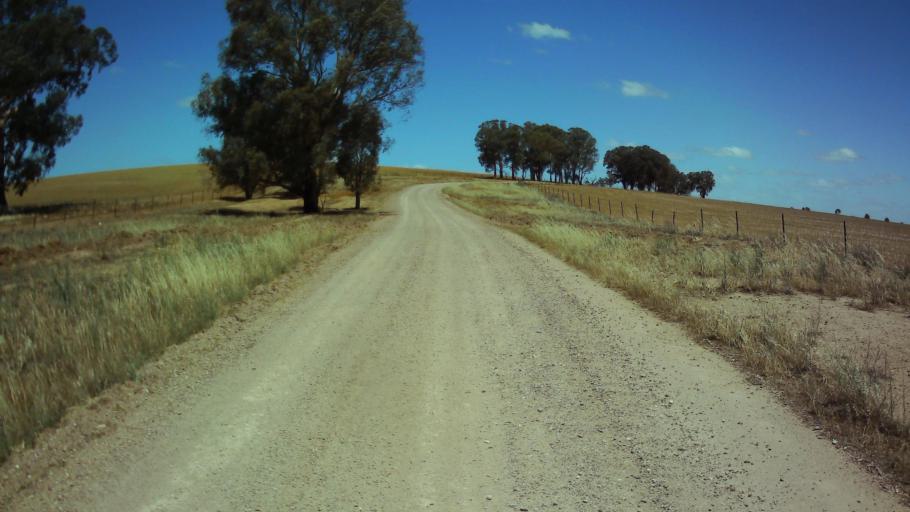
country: AU
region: New South Wales
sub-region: Weddin
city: Grenfell
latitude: -33.9391
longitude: 148.3295
